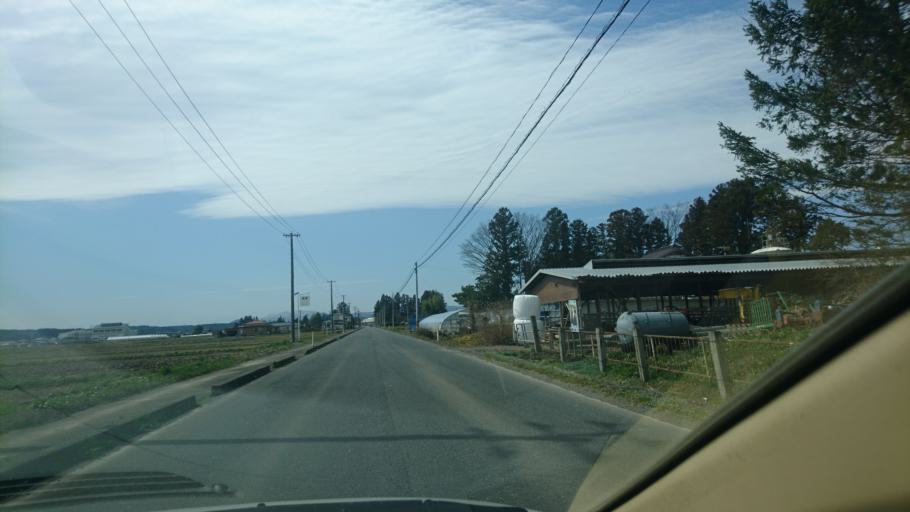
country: JP
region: Miyagi
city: Furukawa
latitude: 38.7404
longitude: 140.9665
